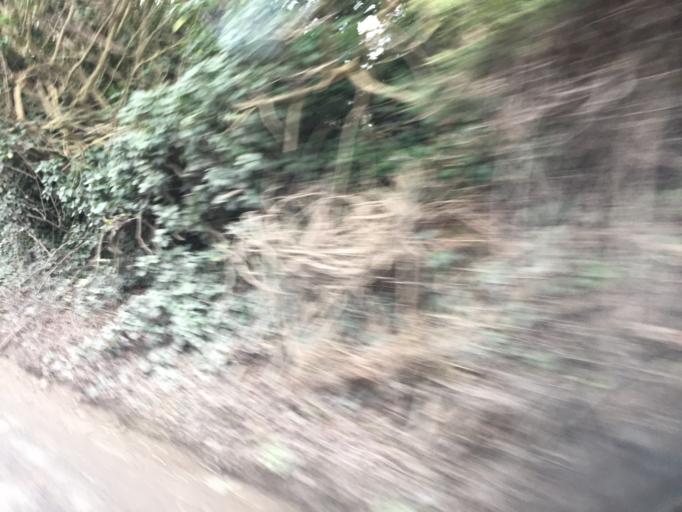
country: GB
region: England
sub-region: Oxfordshire
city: Wantage
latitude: 51.5907
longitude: -1.4390
